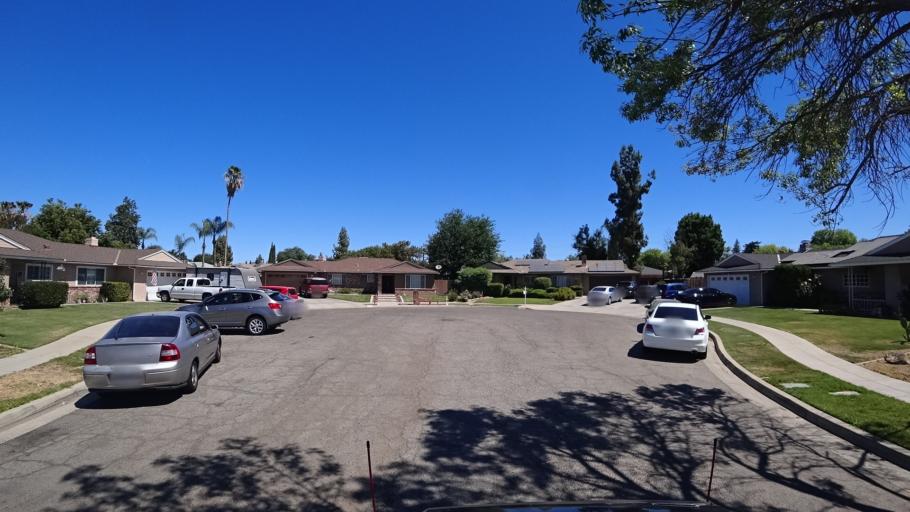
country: US
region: California
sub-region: Fresno County
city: West Park
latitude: 36.8016
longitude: -119.8502
